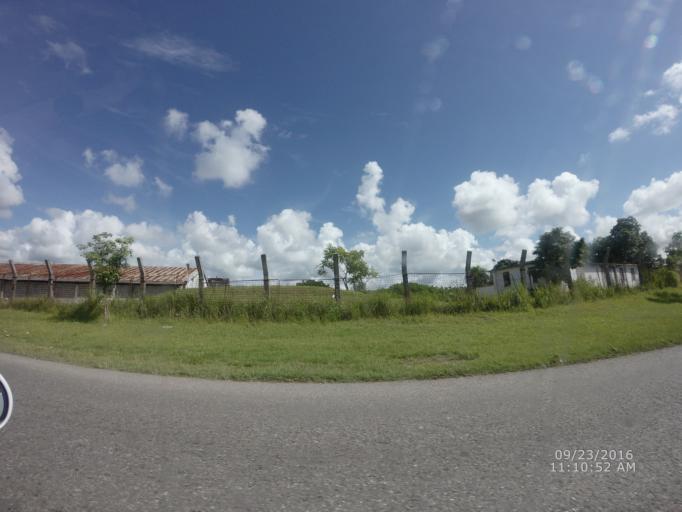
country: CU
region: La Habana
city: Arroyo Naranjo
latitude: 23.0230
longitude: -82.2615
